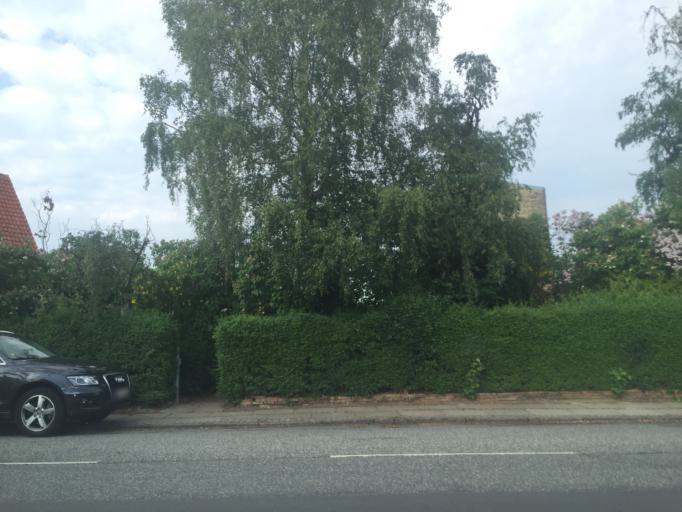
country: DK
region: Capital Region
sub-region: Gentofte Kommune
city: Charlottenlund
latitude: 55.7409
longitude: 12.5496
